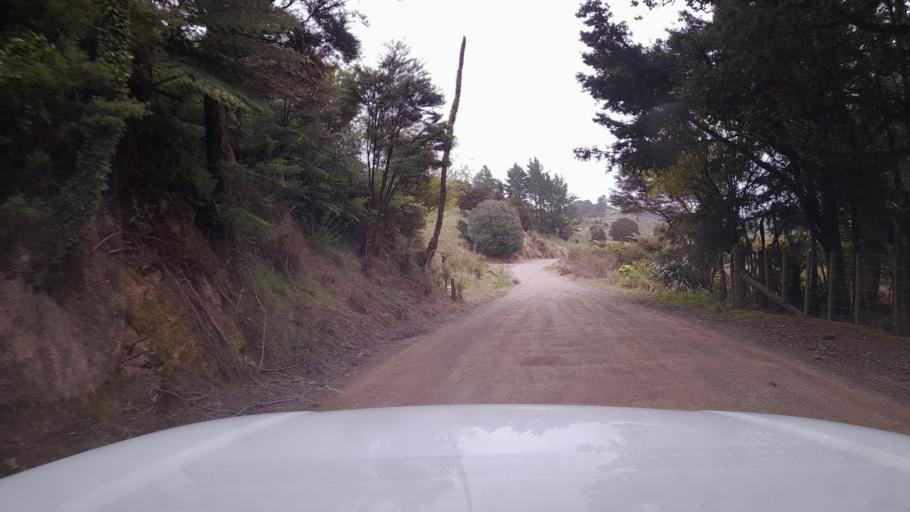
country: NZ
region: Northland
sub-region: Far North District
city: Paihia
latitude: -35.3416
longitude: 174.2338
